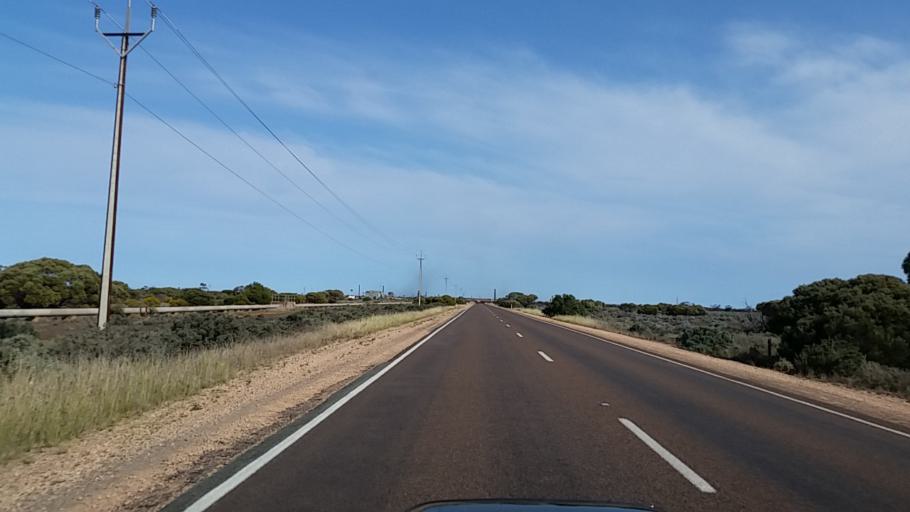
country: AU
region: South Australia
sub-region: Whyalla
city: Whyalla
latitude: -32.9702
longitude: 137.5790
